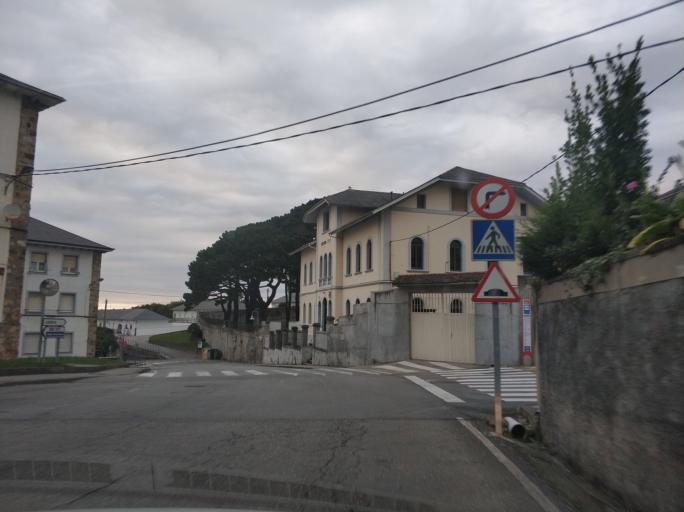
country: ES
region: Asturias
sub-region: Province of Asturias
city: Navia
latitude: 43.5459
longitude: -6.5297
